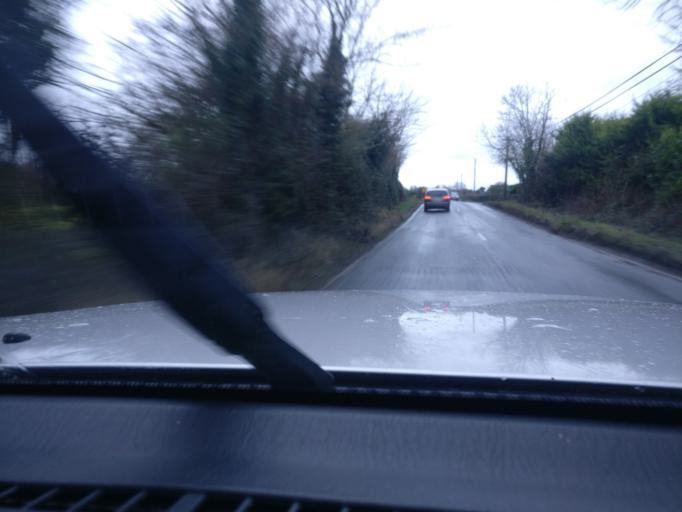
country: IE
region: Leinster
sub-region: An Mhi
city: Longwood
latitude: 53.4664
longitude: -6.9126
